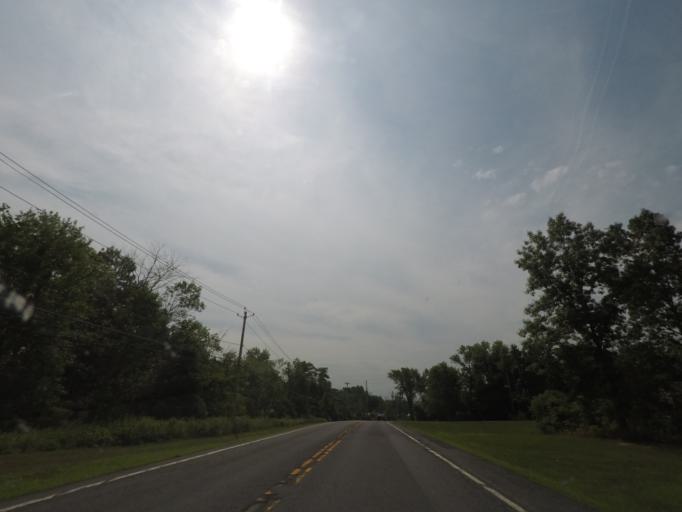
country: US
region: New York
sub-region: Saratoga County
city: Mechanicville
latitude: 42.8761
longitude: -73.6800
